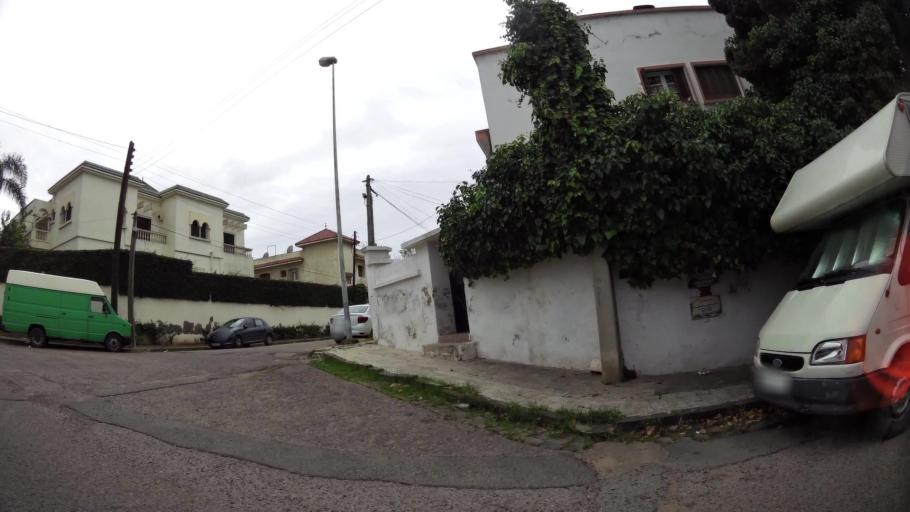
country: MA
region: Grand Casablanca
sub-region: Casablanca
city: Casablanca
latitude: 33.5630
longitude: -7.6218
